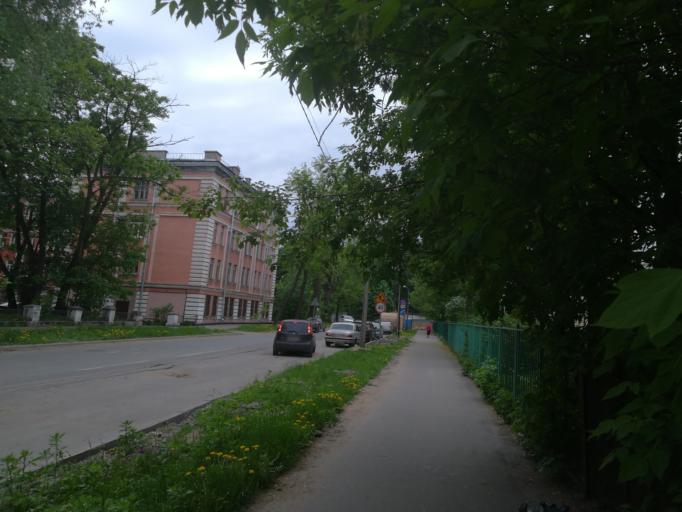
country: RU
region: St.-Petersburg
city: Vasyl'evsky Ostrov
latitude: 59.9517
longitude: 30.2579
